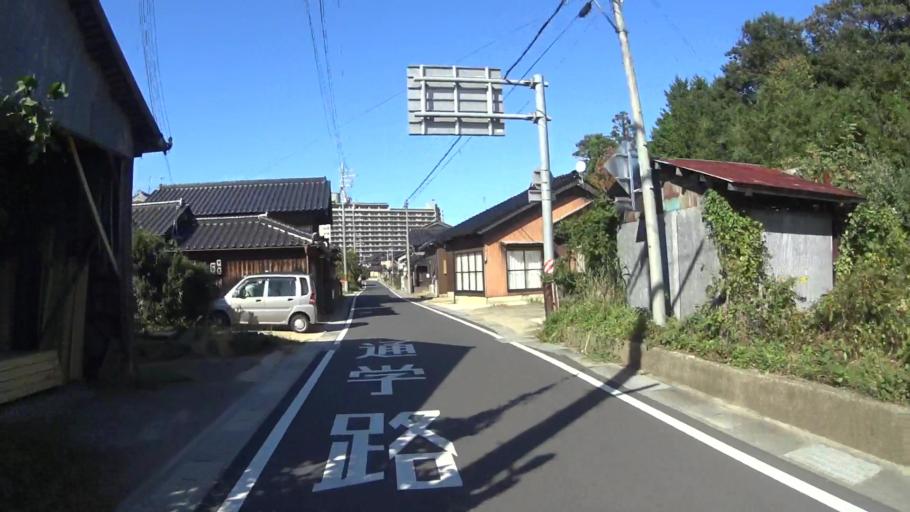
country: JP
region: Hyogo
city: Toyooka
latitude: 35.6326
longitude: 134.9291
